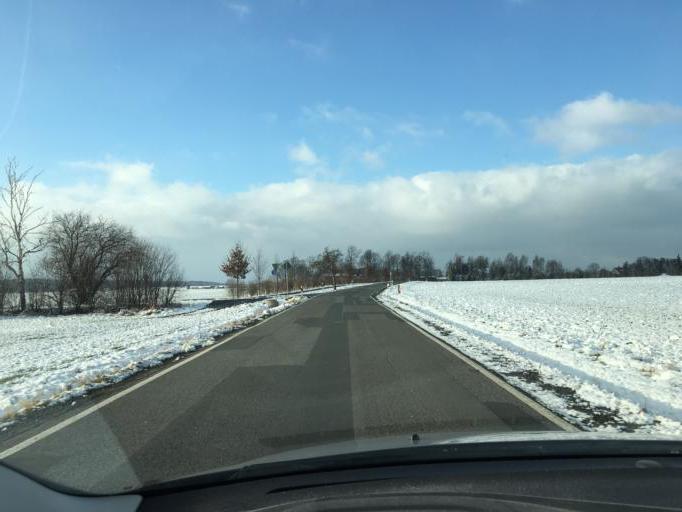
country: DE
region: Saxony
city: Grimma
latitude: 51.2536
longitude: 12.6974
